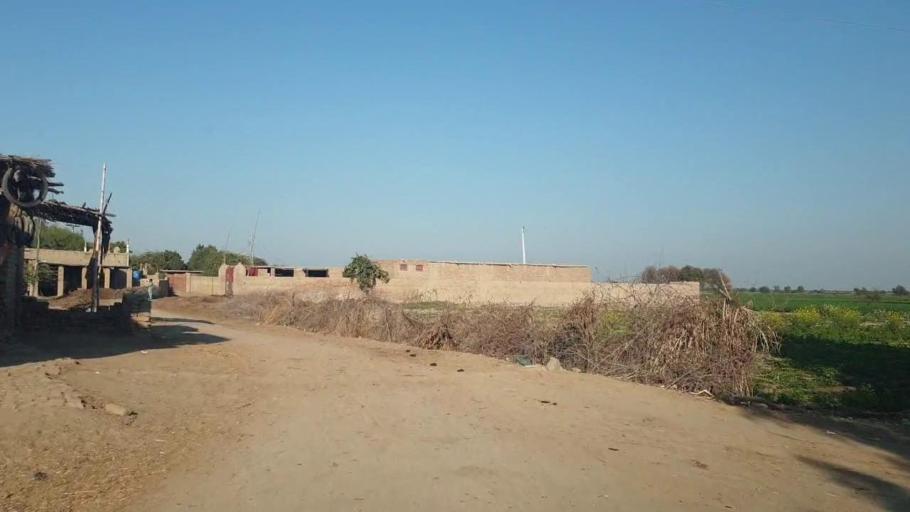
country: PK
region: Sindh
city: Shahdadpur
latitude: 26.0219
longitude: 68.6792
